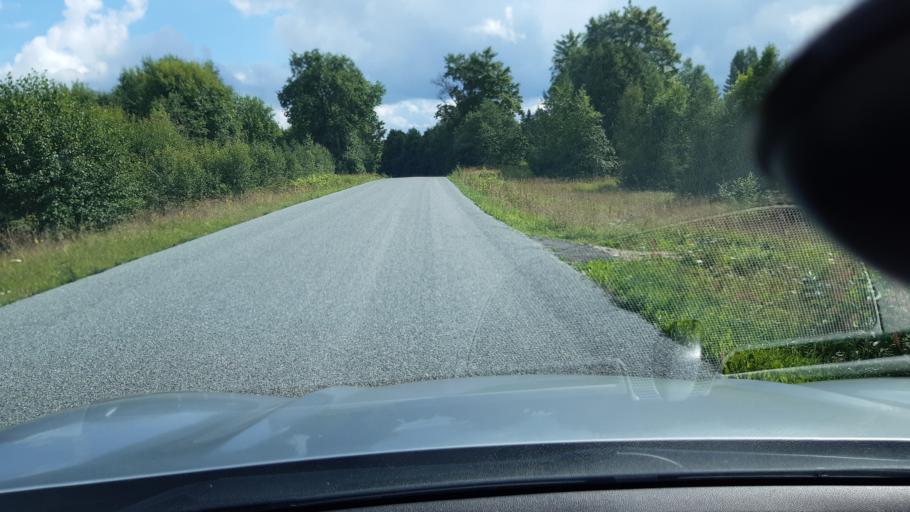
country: EE
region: Raplamaa
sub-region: Kehtna vald
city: Kehtna
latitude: 58.9047
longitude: 25.0566
